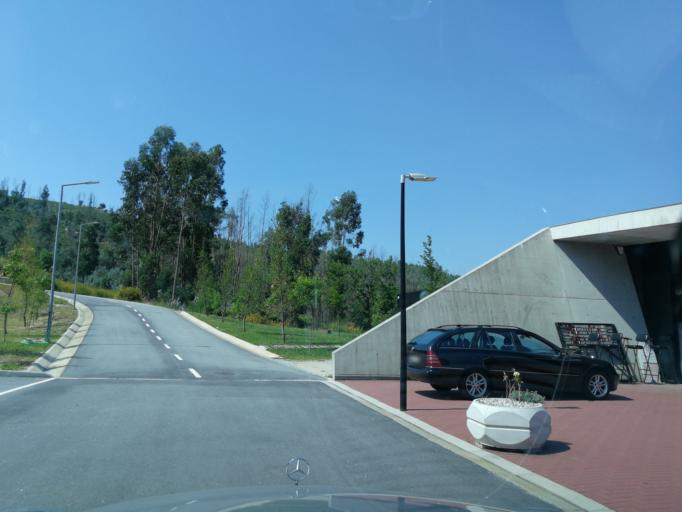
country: PT
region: Braga
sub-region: Braga
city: Adaufe
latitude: 41.5639
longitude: -8.3593
